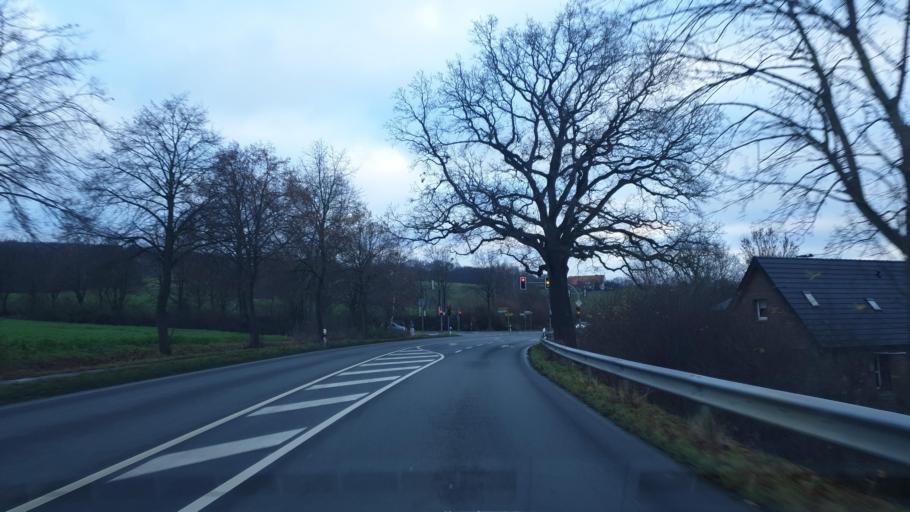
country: DE
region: North Rhine-Westphalia
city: Loehne
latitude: 52.1607
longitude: 8.6849
